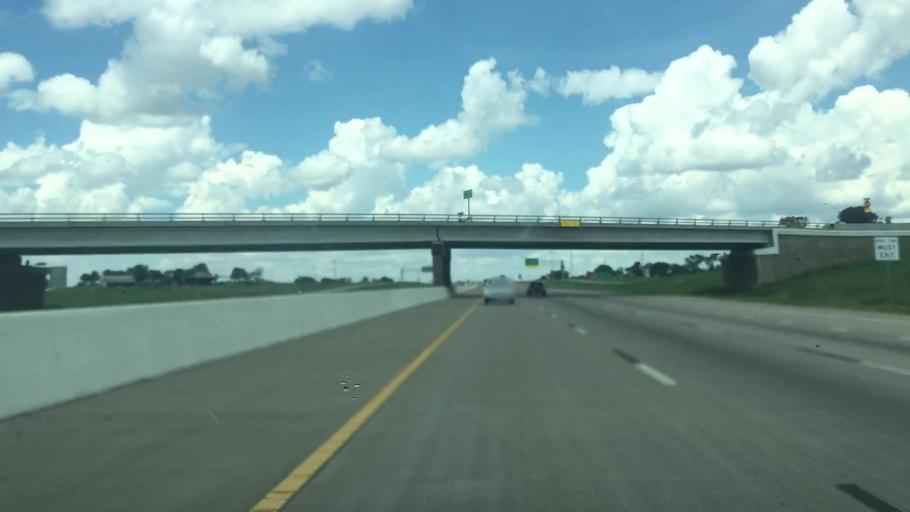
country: US
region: Texas
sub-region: McLennan County
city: West
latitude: 31.8376
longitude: -97.0901
